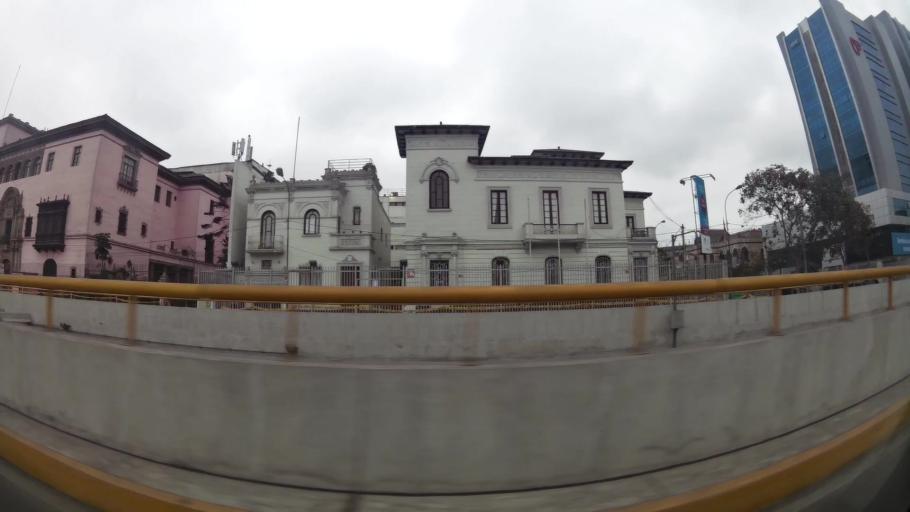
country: PE
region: Lima
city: Lima
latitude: -12.0654
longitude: -77.0373
